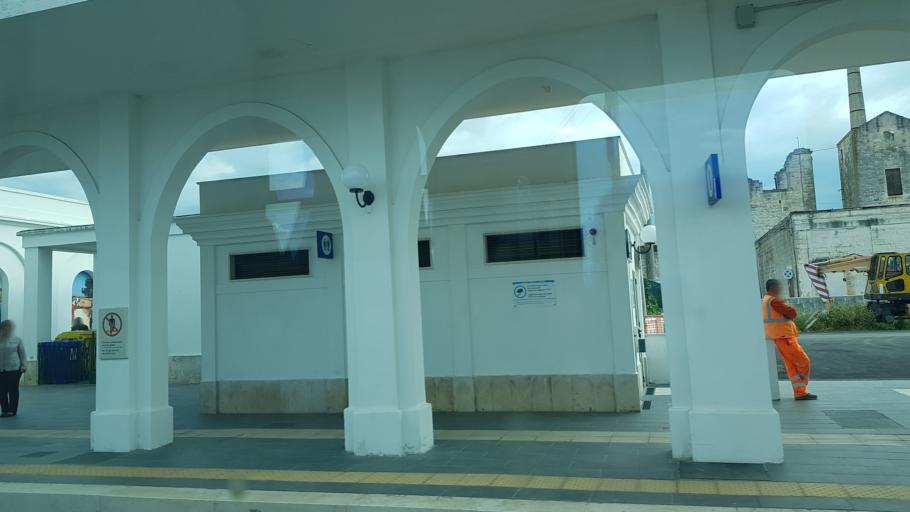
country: IT
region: Apulia
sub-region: Provincia di Brindisi
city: Ostuni
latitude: 40.7524
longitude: 17.5804
